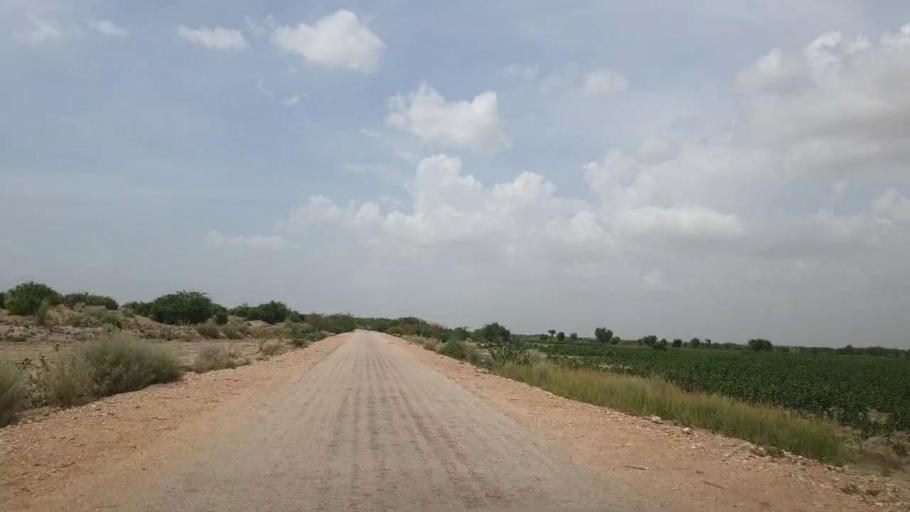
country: PK
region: Sindh
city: Kot Diji
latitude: 27.2309
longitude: 69.0890
